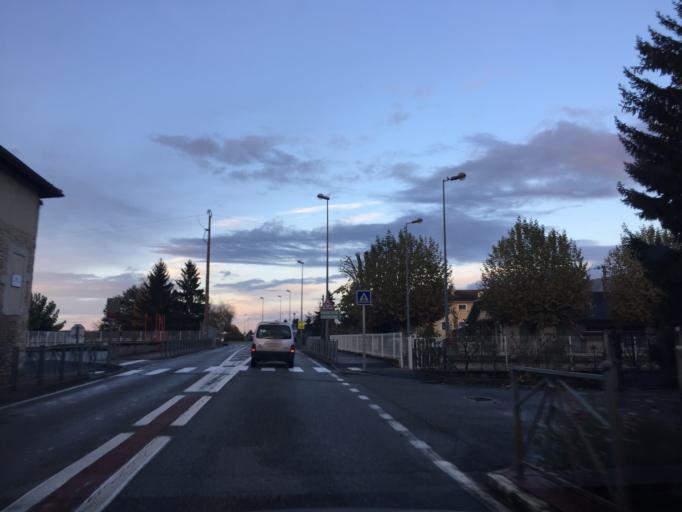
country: FR
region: Rhone-Alpes
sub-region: Departement de l'Isere
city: Saint-Just-de-Claix
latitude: 45.0751
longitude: 5.2838
